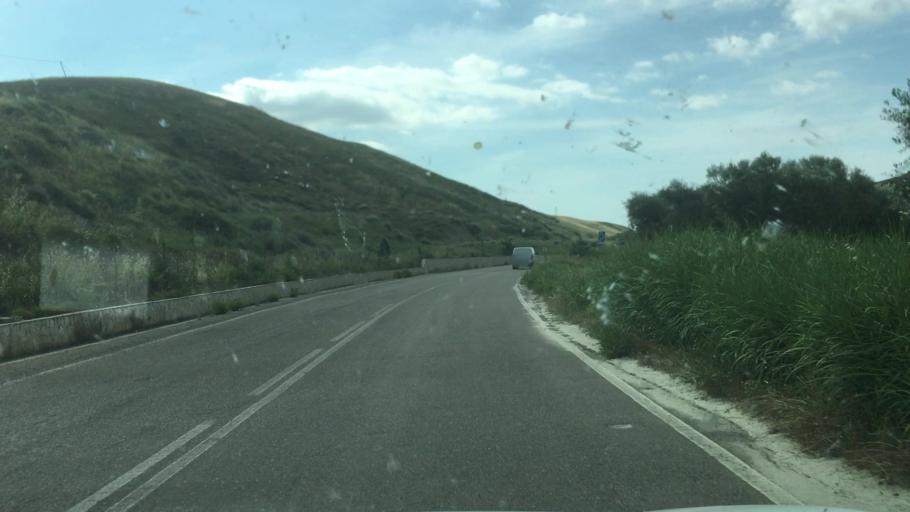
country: IT
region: Basilicate
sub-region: Provincia di Matera
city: Salandra
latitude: 40.5331
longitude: 16.2867
